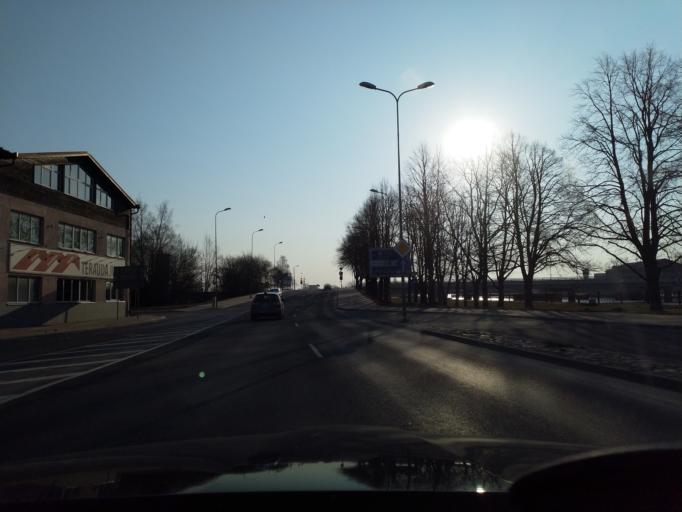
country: LV
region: Liepaja
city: Liepaja
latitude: 56.5134
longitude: 21.0196
